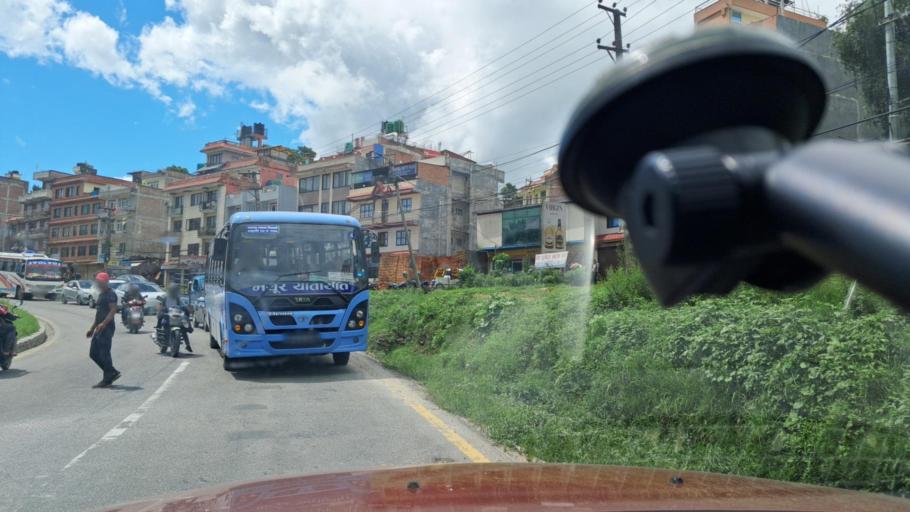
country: NP
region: Central Region
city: Banepa
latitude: 27.6251
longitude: 85.5484
